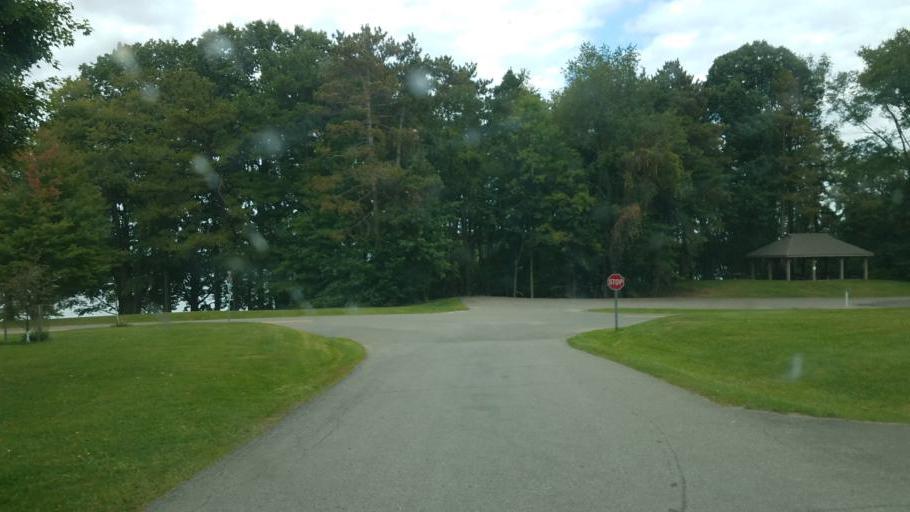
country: US
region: Pennsylvania
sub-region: Crawford County
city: Pymatuning Central
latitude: 41.5007
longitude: -80.4570
